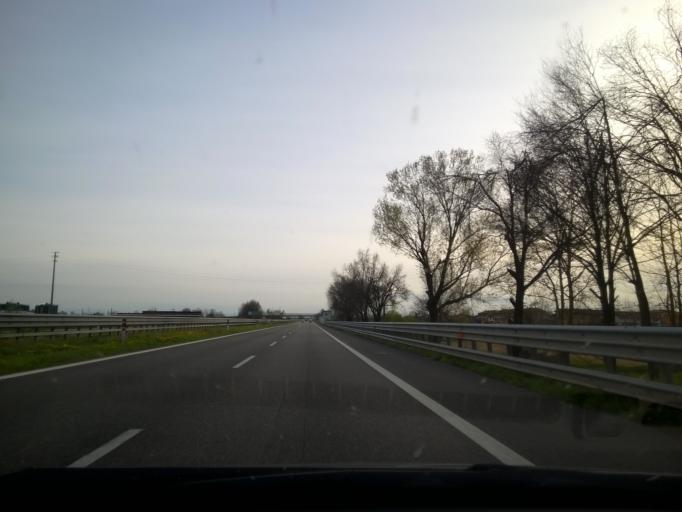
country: IT
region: Lombardy
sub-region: Provincia di Cremona
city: Dosimo
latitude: 45.1697
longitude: 10.0835
